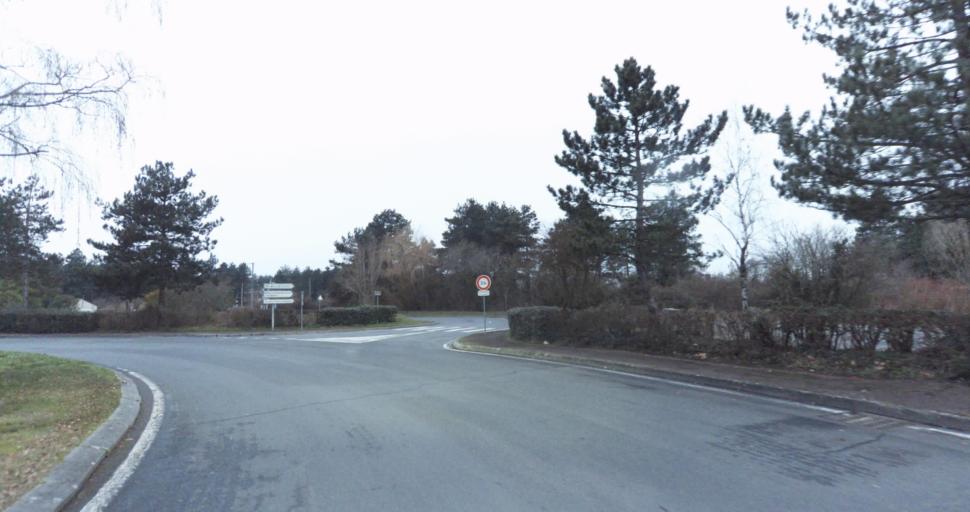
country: FR
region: Pays de la Loire
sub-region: Departement de Maine-et-Loire
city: Distre
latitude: 47.2386
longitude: -0.1030
